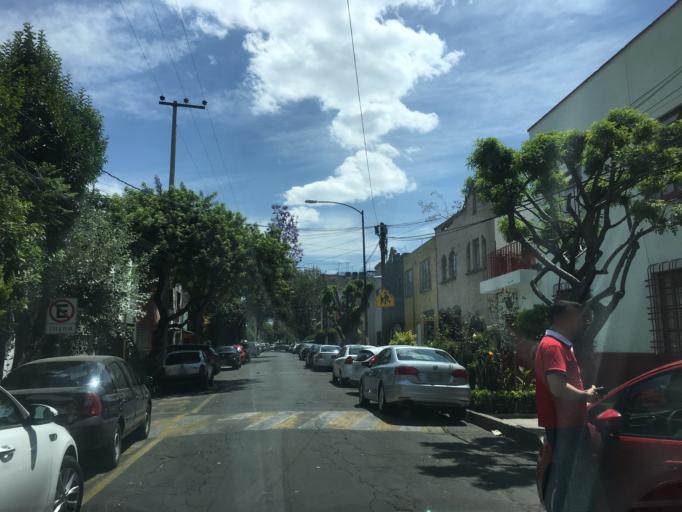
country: MX
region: Mexico City
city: Benito Juarez
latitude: 19.3976
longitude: -99.1568
